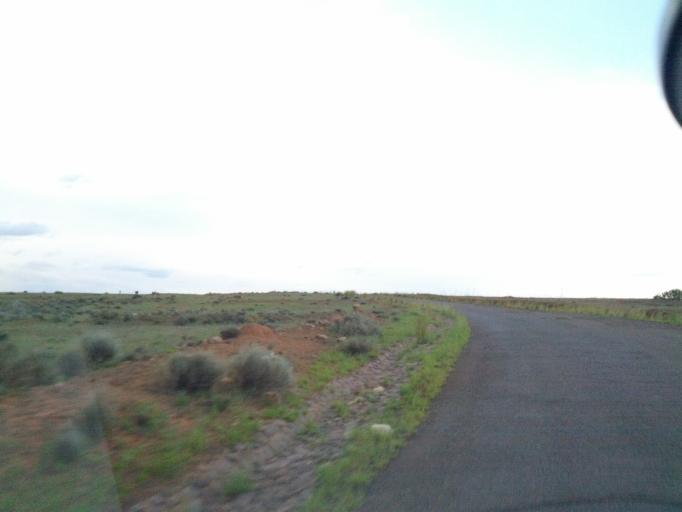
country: LS
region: Qacha's Nek
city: Qacha's Nek
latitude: -30.0519
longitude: 28.3760
